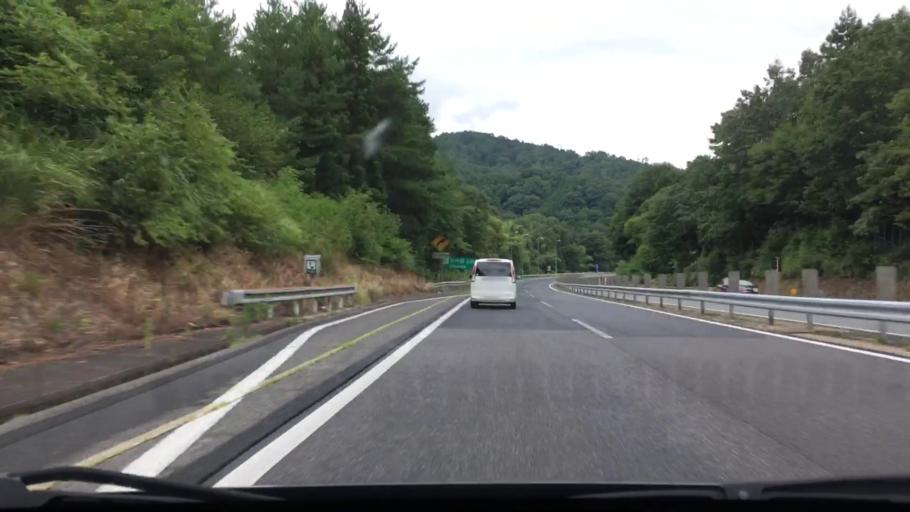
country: JP
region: Hiroshima
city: Hiroshima-shi
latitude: 34.6815
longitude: 132.5613
